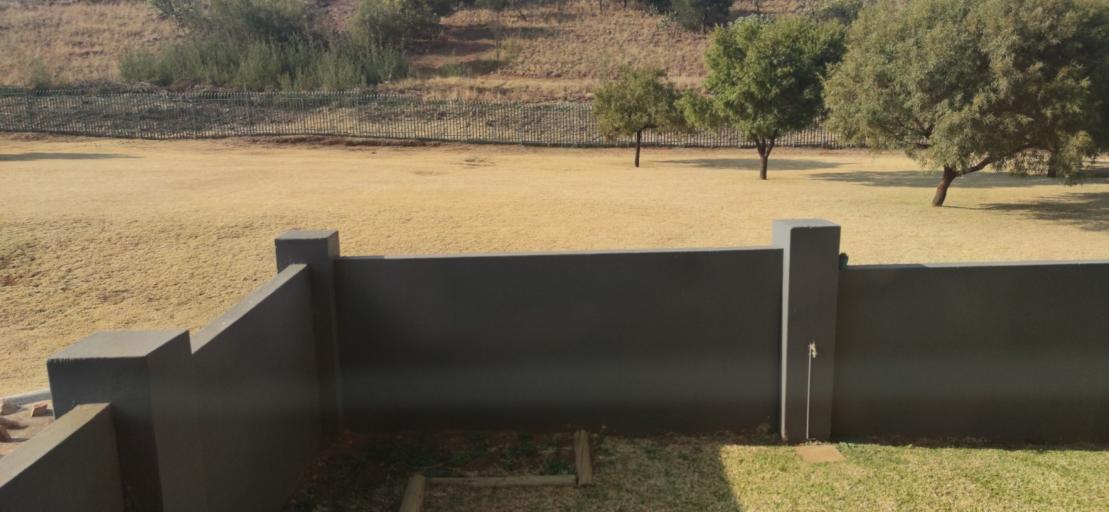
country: ZA
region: Gauteng
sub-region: West Rand District Municipality
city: Krugersdorp
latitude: -26.0861
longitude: 27.8171
